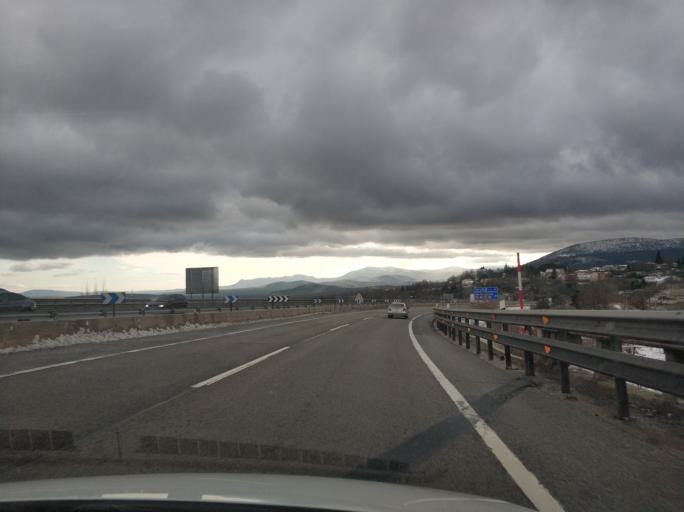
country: ES
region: Madrid
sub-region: Provincia de Madrid
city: Robregordo
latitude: 41.1084
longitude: -3.5888
